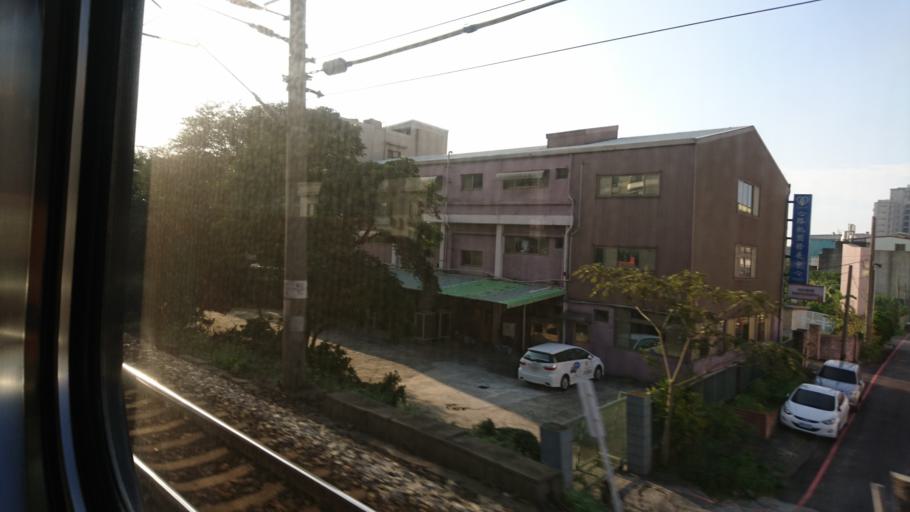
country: TW
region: Taiwan
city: Daxi
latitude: 24.9413
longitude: 121.2130
